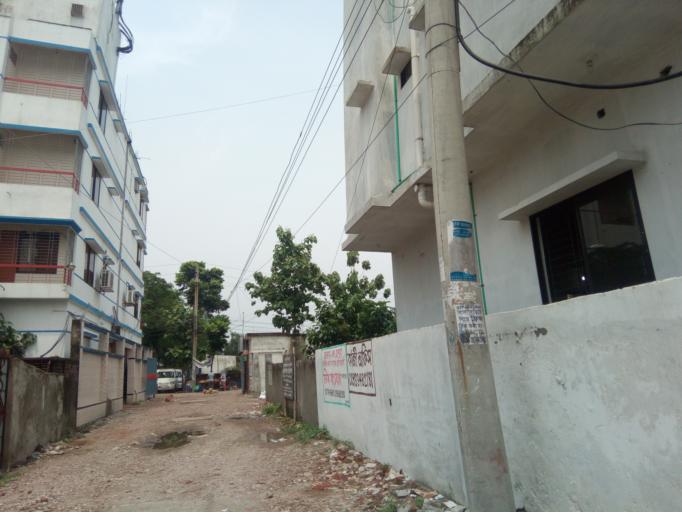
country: BD
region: Dhaka
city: Azimpur
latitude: 23.7447
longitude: 90.3515
